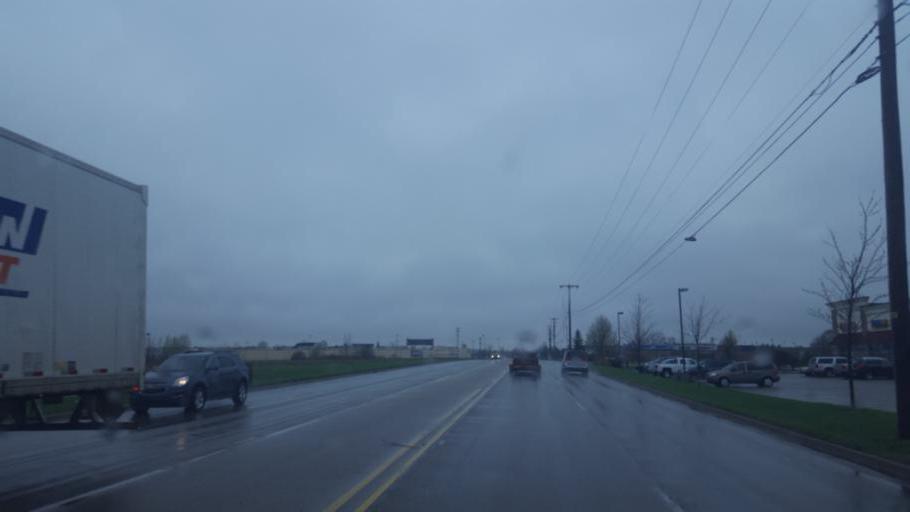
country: US
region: Michigan
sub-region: Isabella County
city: Mount Pleasant
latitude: 43.5754
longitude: -84.7584
